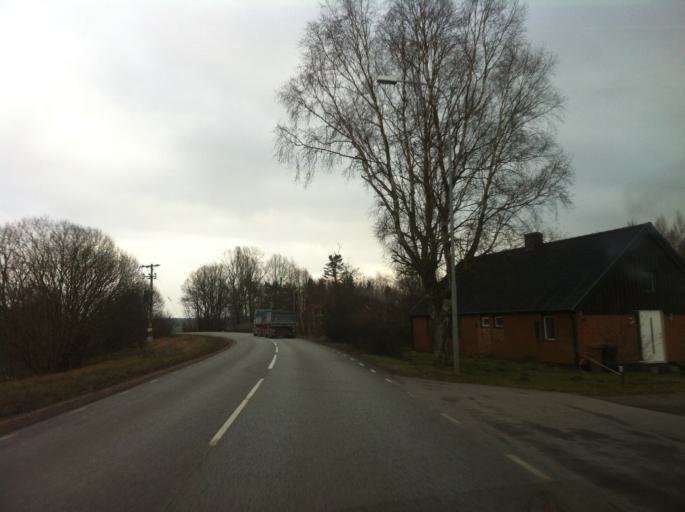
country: SE
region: Skane
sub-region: Kavlinge Kommun
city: Hofterup
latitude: 55.8319
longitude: 12.9714
